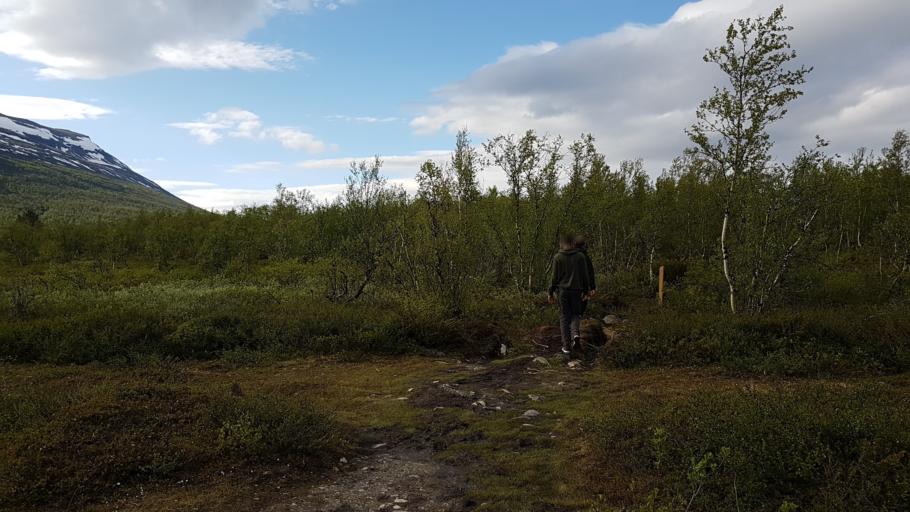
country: NO
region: Troms
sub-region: Bardu
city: Setermoen
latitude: 68.3474
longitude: 18.7802
